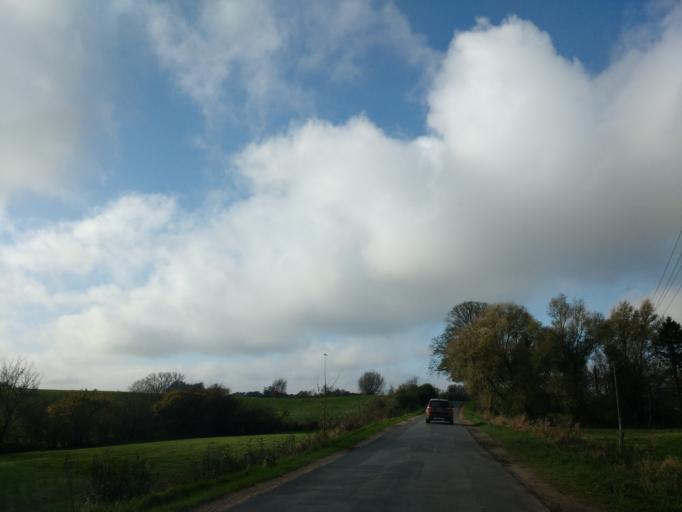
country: DE
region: Mecklenburg-Vorpommern
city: Kalkhorst
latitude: 53.9305
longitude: 11.0943
